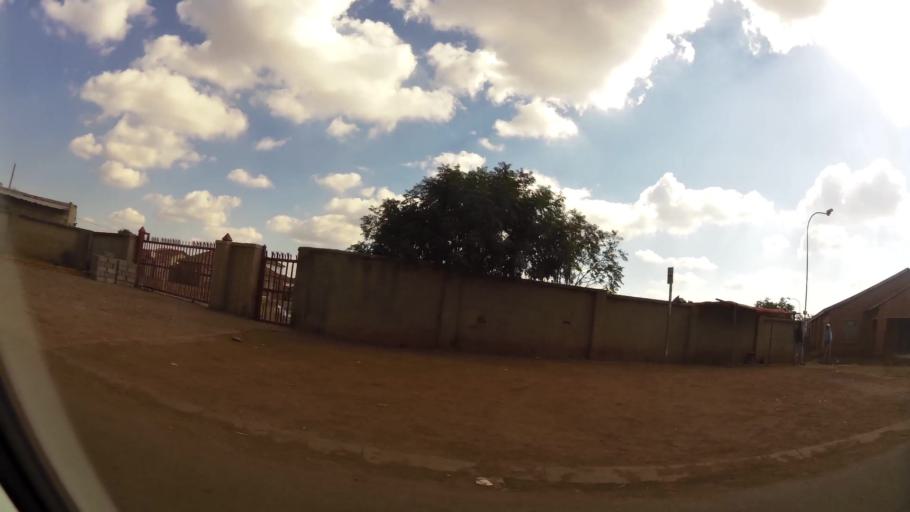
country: ZA
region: Gauteng
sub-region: City of Tshwane Metropolitan Municipality
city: Cullinan
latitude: -25.7007
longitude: 28.4110
